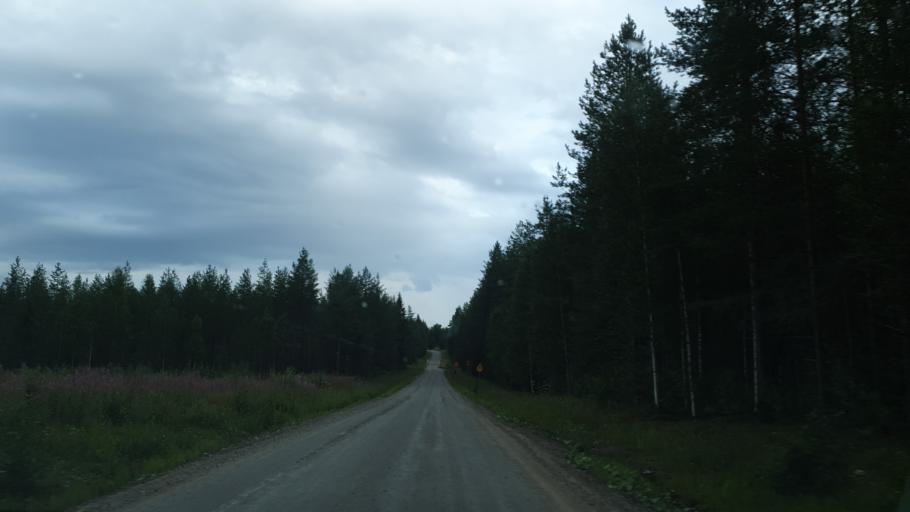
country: FI
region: Kainuu
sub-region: Kehys-Kainuu
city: Kuhmo
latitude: 64.2105
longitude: 29.3699
